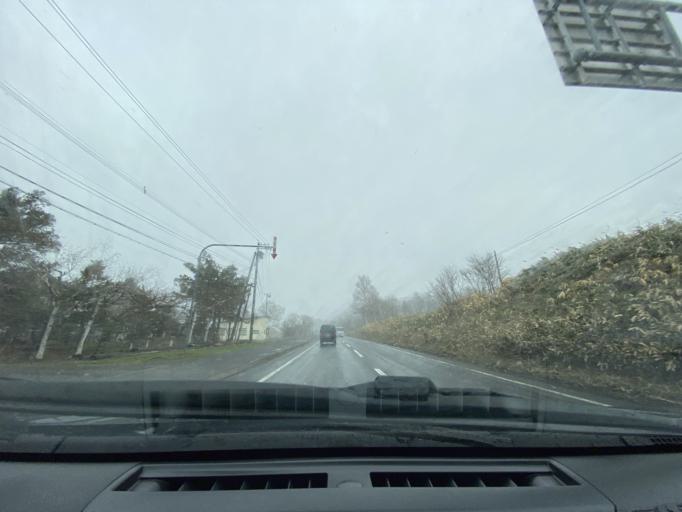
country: JP
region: Hokkaido
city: Fukagawa
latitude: 43.7100
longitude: 142.1413
